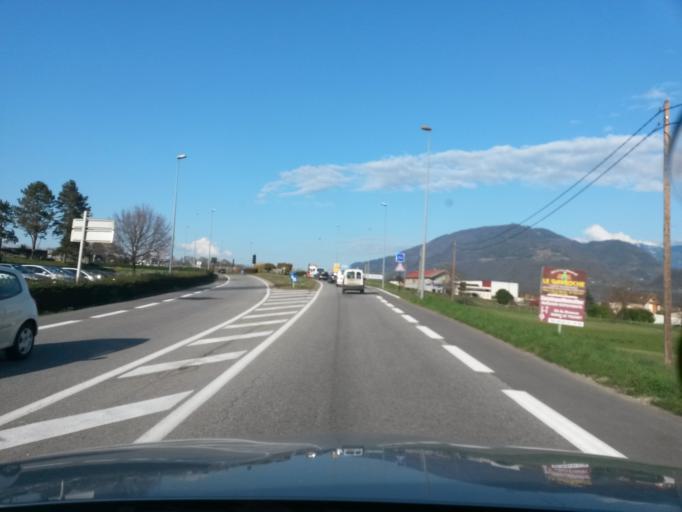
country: FR
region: Rhone-Alpes
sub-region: Departement de l'Isere
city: Le Touvet
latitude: 45.3564
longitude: 5.9541
